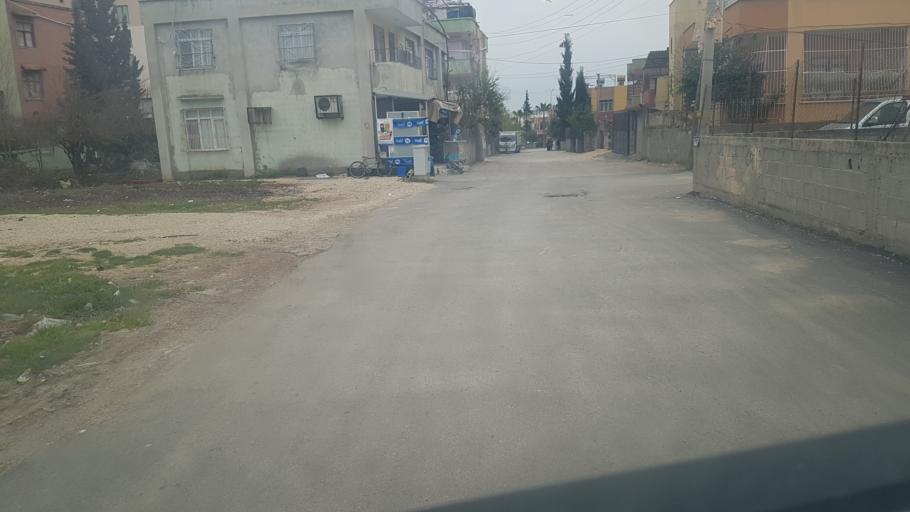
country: TR
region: Adana
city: Seyhan
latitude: 37.0225
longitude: 35.2736
